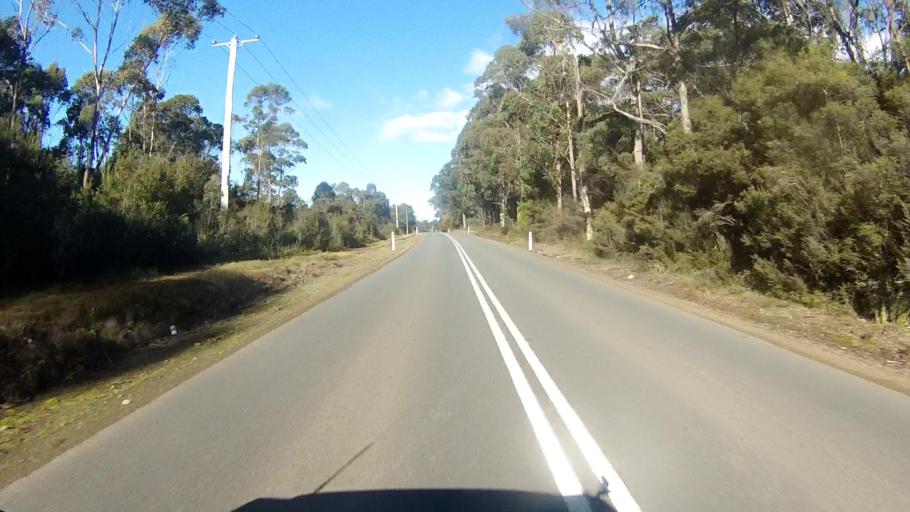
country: AU
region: Tasmania
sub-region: Clarence
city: Sandford
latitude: -43.0824
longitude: 147.8651
